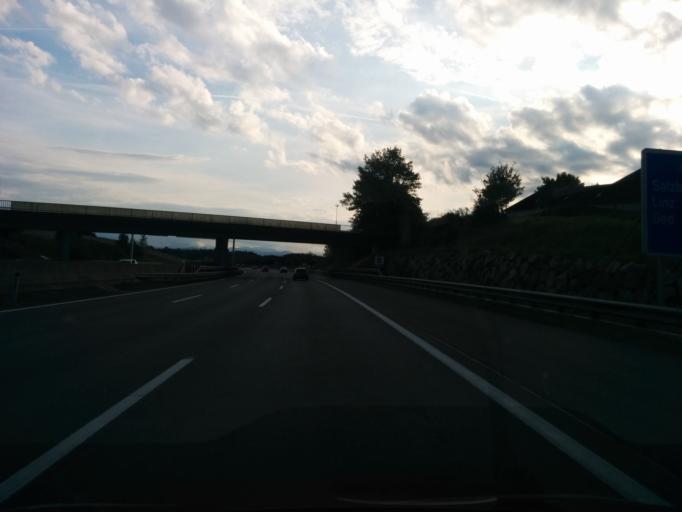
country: AT
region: Lower Austria
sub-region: Politischer Bezirk Amstetten
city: Zeillern
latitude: 48.1339
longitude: 14.8320
